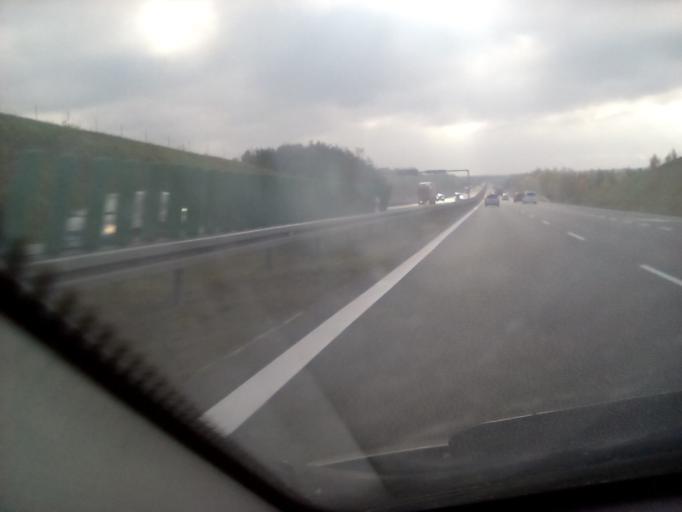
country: PL
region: Masovian Voivodeship
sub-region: Powiat bialobrzeski
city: Promna
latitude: 51.6737
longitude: 20.9465
